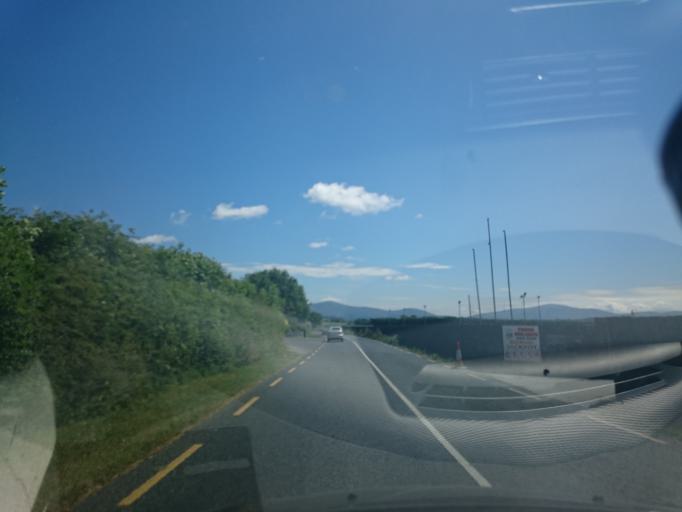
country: IE
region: Leinster
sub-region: County Carlow
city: Bagenalstown
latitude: 52.6321
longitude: -7.0537
